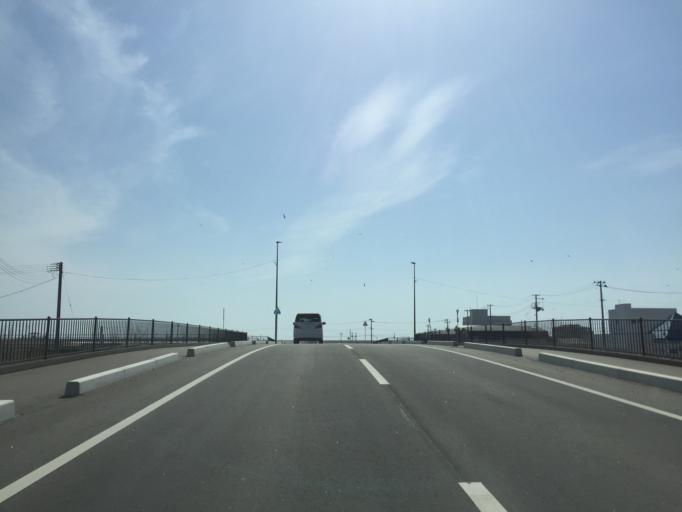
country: JP
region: Miyagi
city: Watari
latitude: 38.0407
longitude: 140.9125
